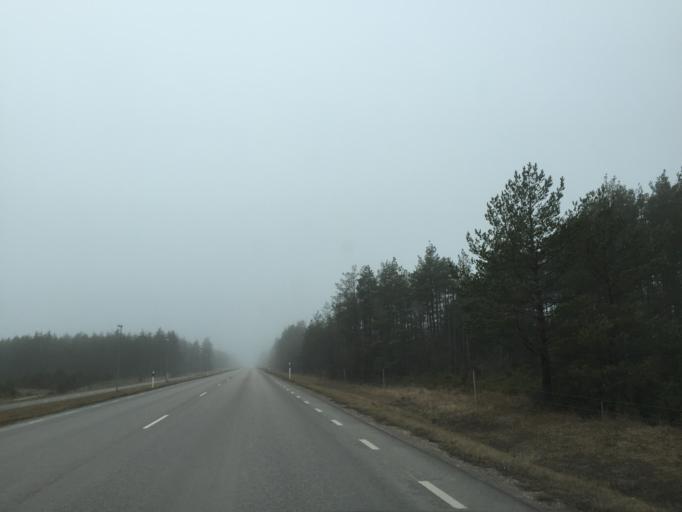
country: EE
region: Saare
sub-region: Kuressaare linn
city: Kuressaare
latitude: 58.2378
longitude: 22.4352
